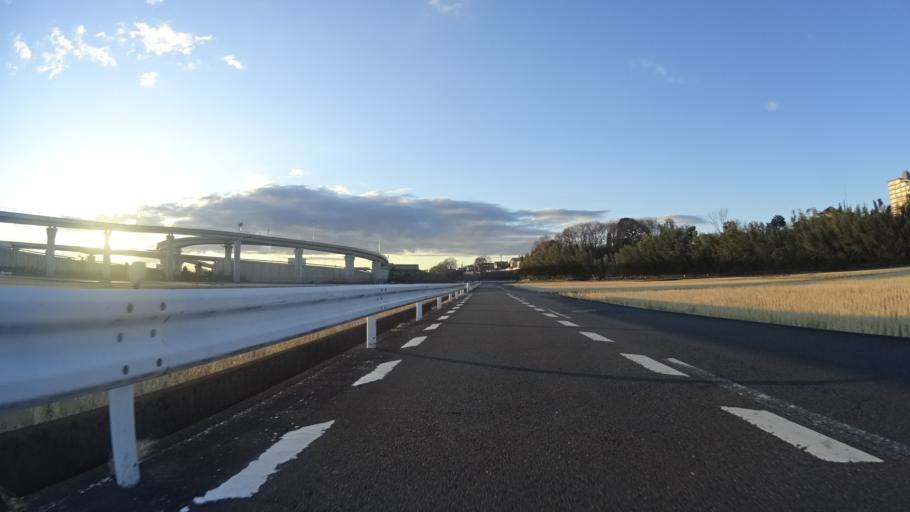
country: JP
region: Kanagawa
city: Zama
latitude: 35.4815
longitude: 139.3706
